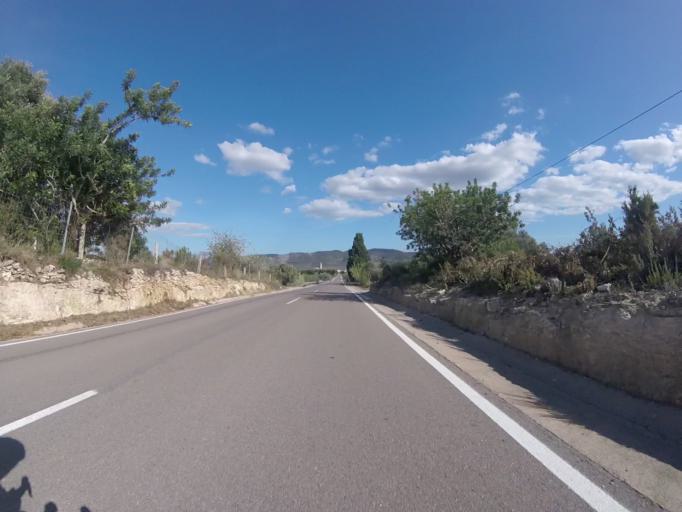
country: ES
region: Valencia
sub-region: Provincia de Castello
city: Alcala de Xivert
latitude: 40.3025
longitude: 0.2037
